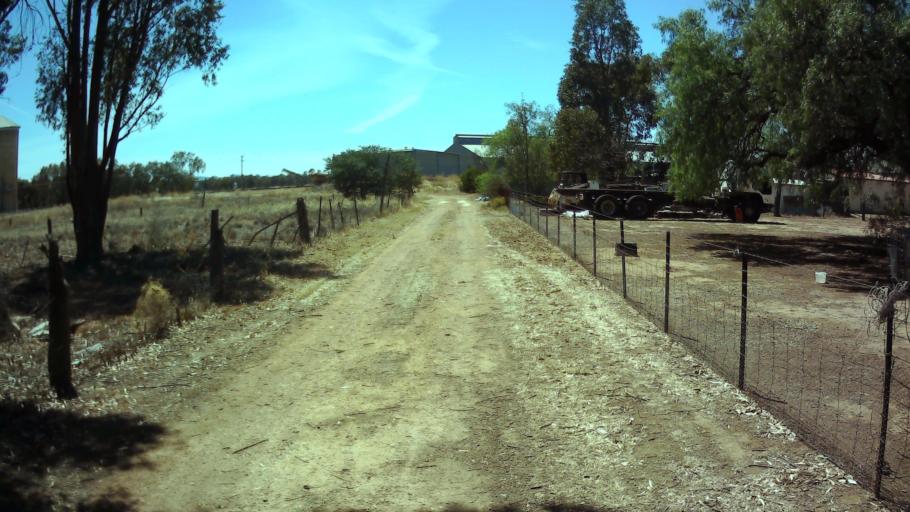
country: AU
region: New South Wales
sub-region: Weddin
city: Grenfell
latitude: -34.0129
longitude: 147.7950
